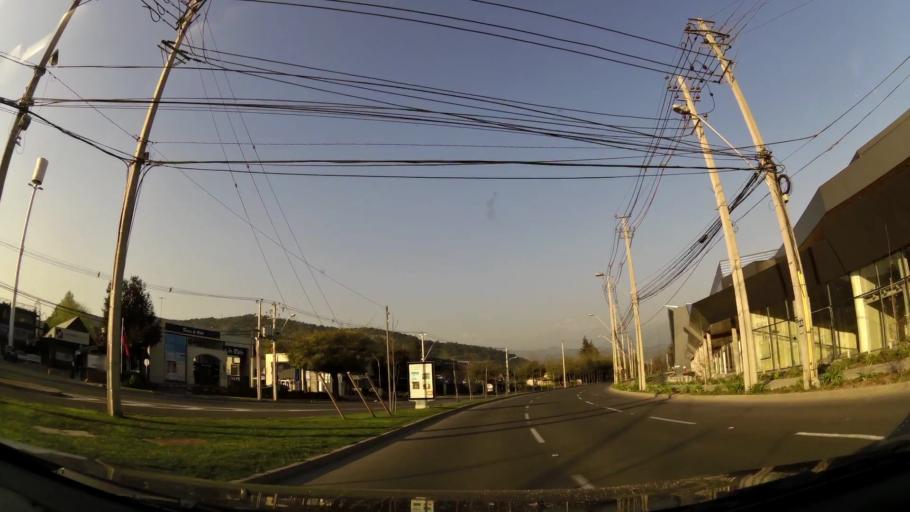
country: CL
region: Santiago Metropolitan
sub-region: Provincia de Santiago
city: Villa Presidente Frei, Nunoa, Santiago, Chile
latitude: -33.3558
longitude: -70.5373
